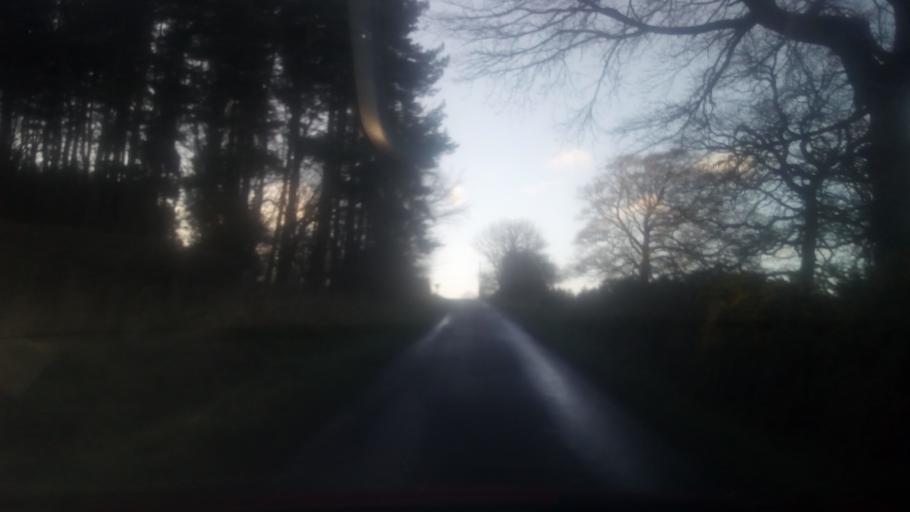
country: GB
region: Scotland
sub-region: The Scottish Borders
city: Jedburgh
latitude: 55.4724
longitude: -2.4497
